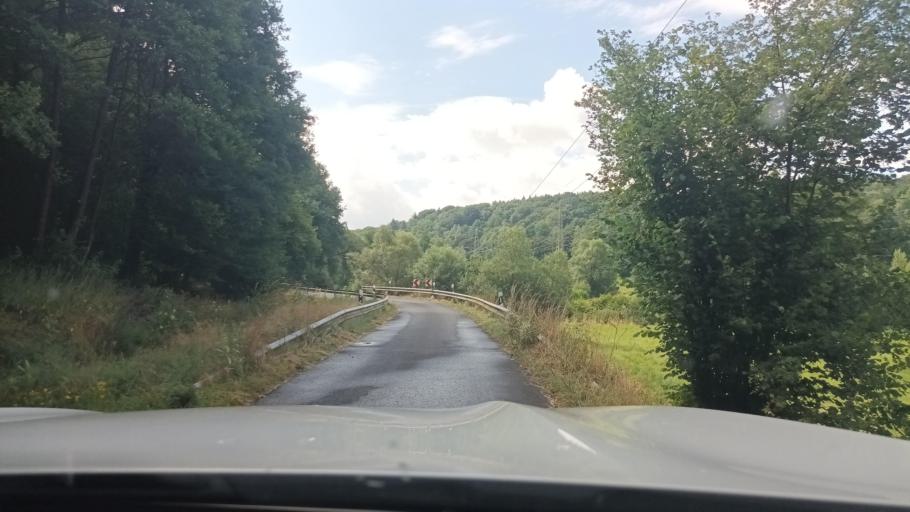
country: DE
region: North Rhine-Westphalia
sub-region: Regierungsbezirk Koln
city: Hennef
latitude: 50.7370
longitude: 7.3162
